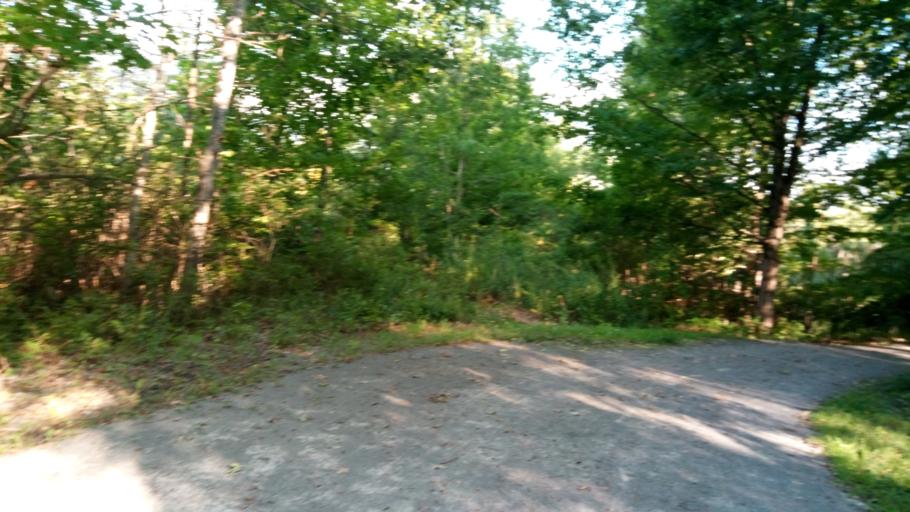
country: US
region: New York
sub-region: Ontario County
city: Victor
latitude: 42.9988
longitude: -77.4403
